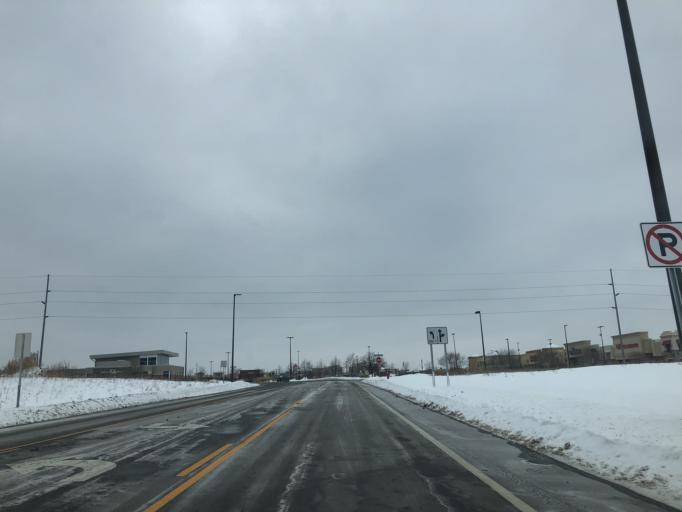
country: US
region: Minnesota
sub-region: Hennepin County
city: Osseo
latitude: 45.0920
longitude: -93.4204
